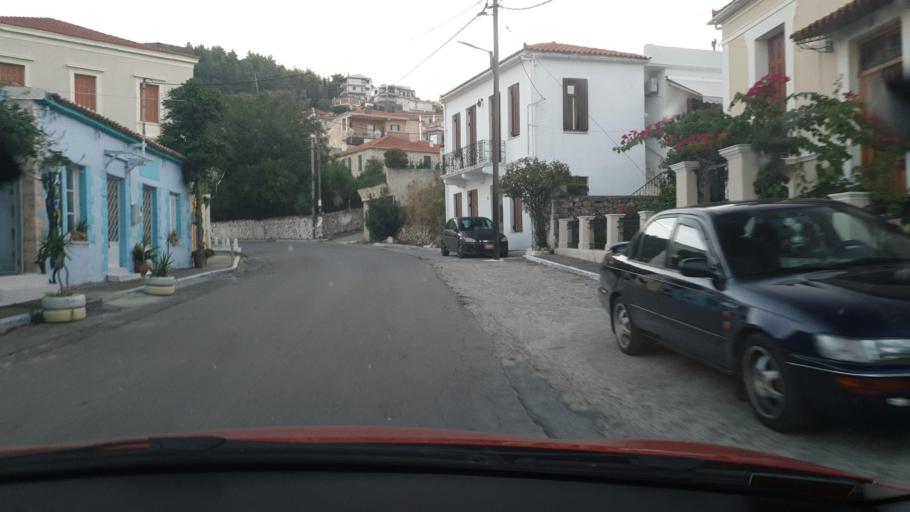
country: GR
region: Central Greece
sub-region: Nomos Evvoias
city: Kymi
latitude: 38.6325
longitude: 24.1050
